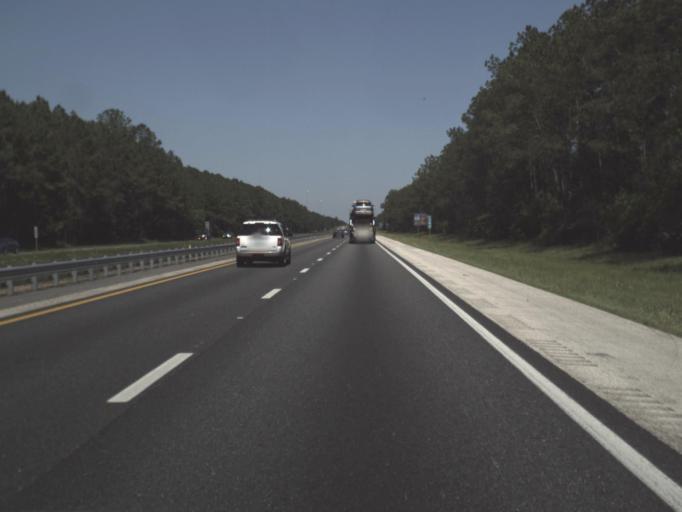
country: US
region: Florida
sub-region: Duval County
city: Baldwin
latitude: 30.2877
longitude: -81.9987
